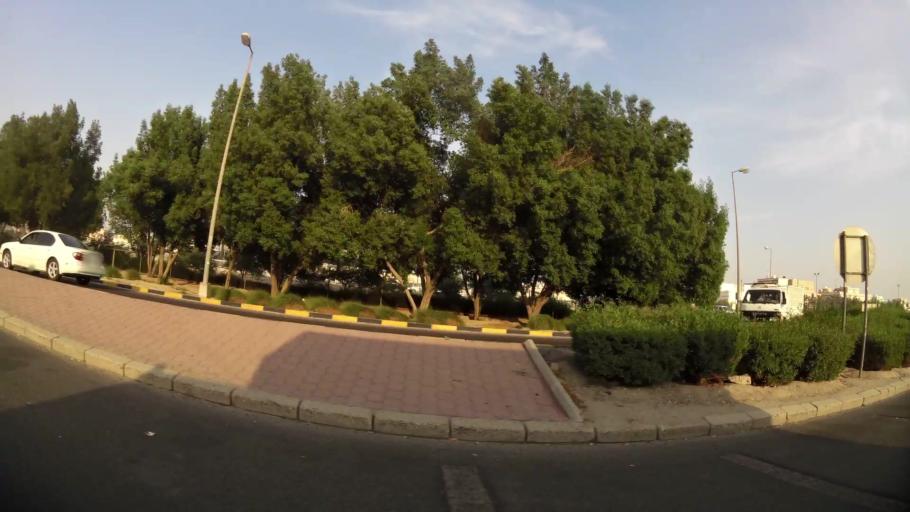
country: KW
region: Mubarak al Kabir
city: Sabah as Salim
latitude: 29.2299
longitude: 48.0530
